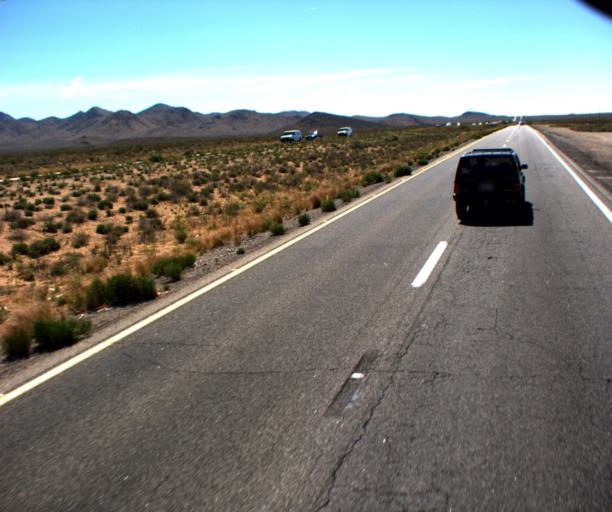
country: US
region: Arizona
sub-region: Mohave County
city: Dolan Springs
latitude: 35.4777
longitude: -114.3167
